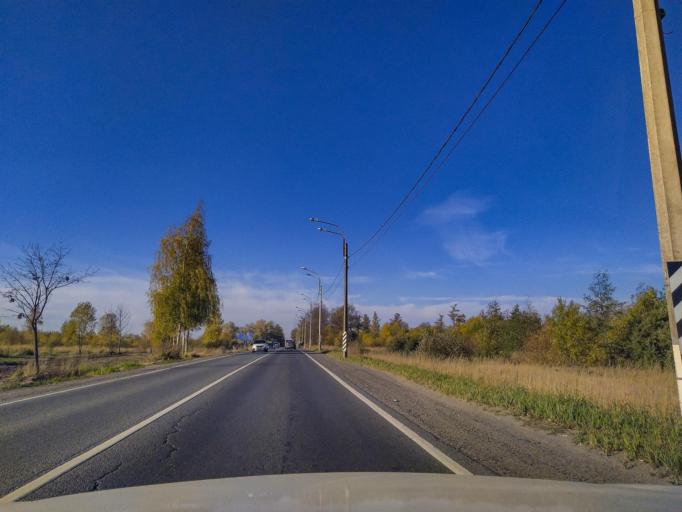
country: RU
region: St.-Petersburg
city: Aleksandrovskaya
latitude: 59.7038
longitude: 30.3488
